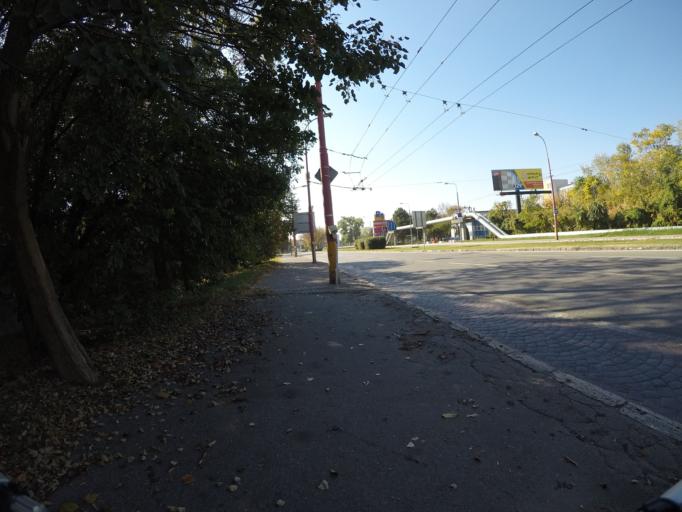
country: SK
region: Bratislavsky
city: Bratislava
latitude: 48.1698
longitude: 17.1587
